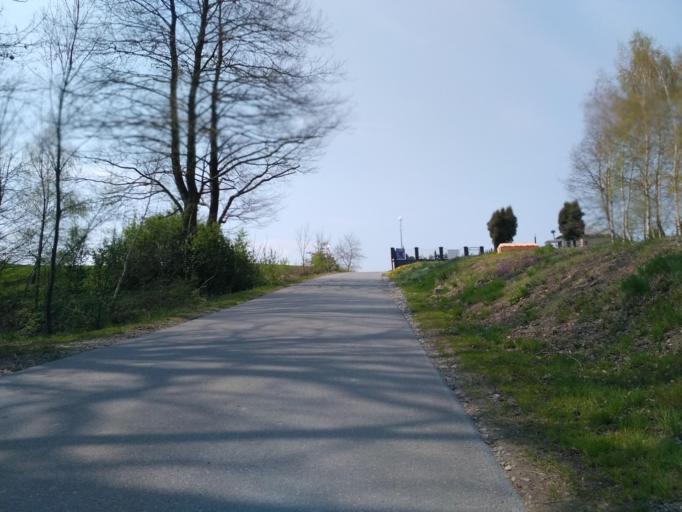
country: PL
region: Subcarpathian Voivodeship
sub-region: Krosno
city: Krosno
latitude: 49.6568
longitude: 21.7481
